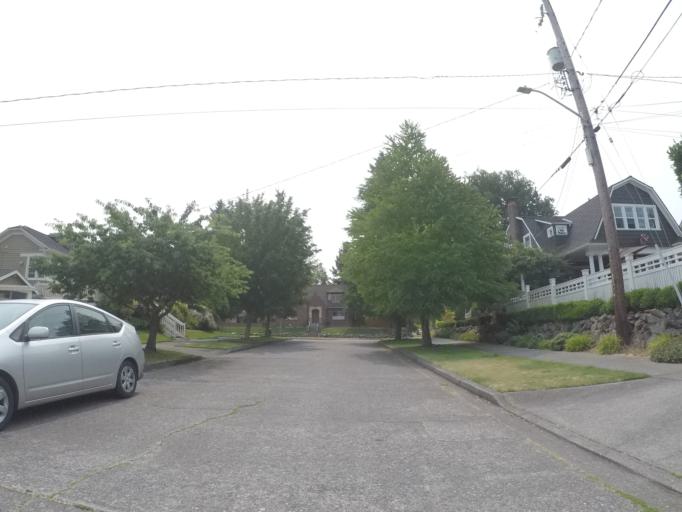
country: US
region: Washington
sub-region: King County
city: Seattle
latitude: 47.5911
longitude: -122.3886
